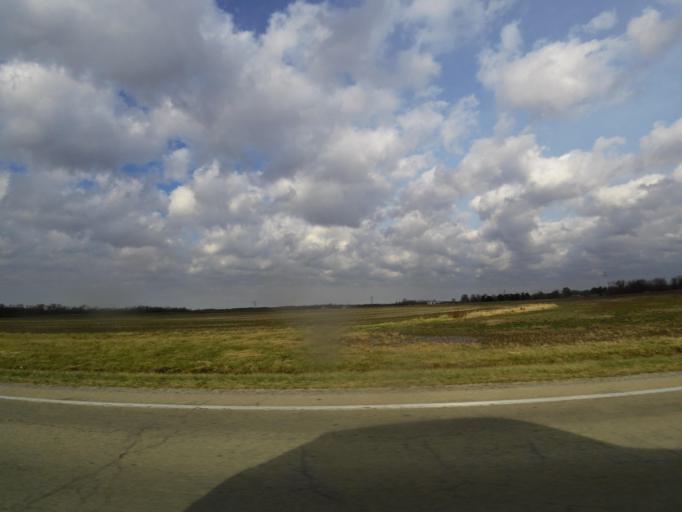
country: US
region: Illinois
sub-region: Fayette County
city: Ramsey
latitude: 39.1526
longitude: -89.1049
